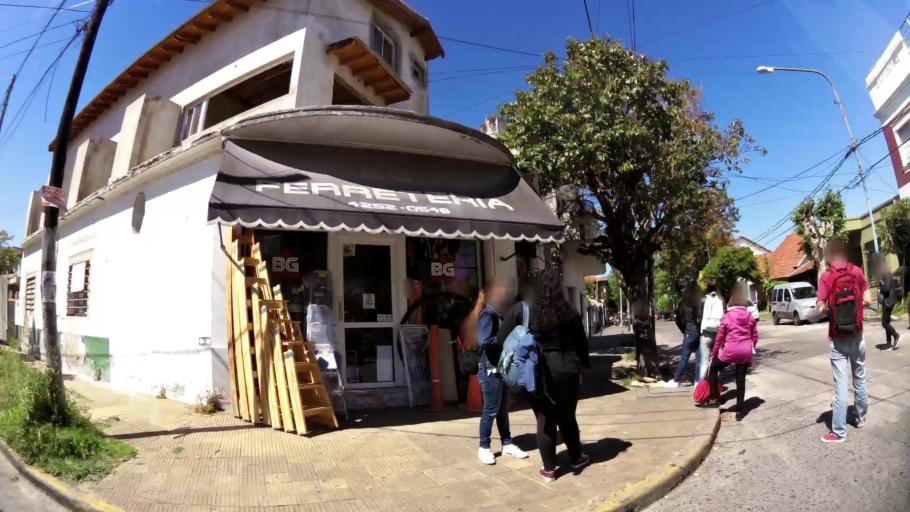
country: AR
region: Buenos Aires
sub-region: Partido de Quilmes
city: Quilmes
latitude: -34.7071
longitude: -58.2764
